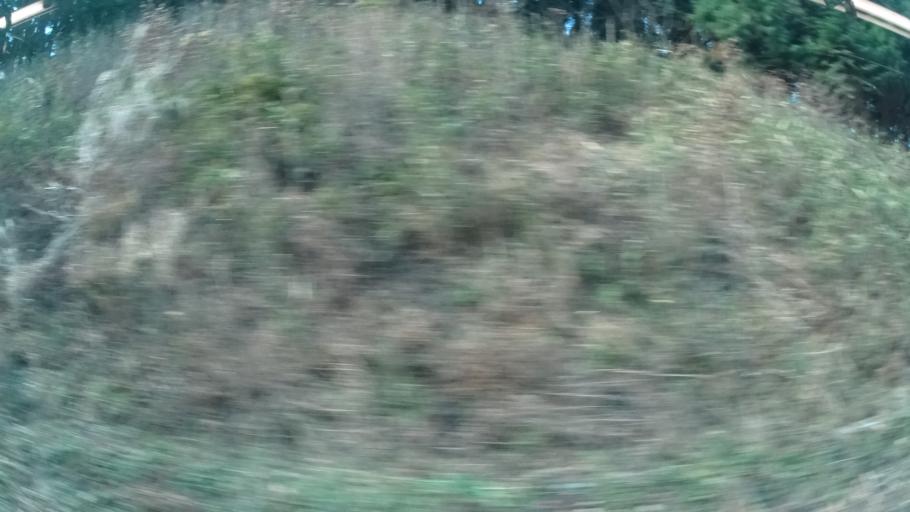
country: JP
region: Miyagi
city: Marumori
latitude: 37.8339
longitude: 140.9254
